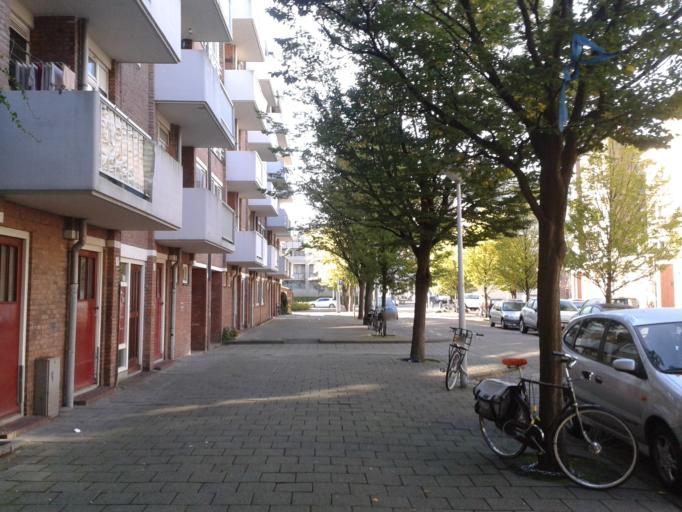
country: NL
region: North Holland
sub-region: Gemeente Amsterdam
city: Amsterdam
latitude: 52.3571
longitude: 4.8284
